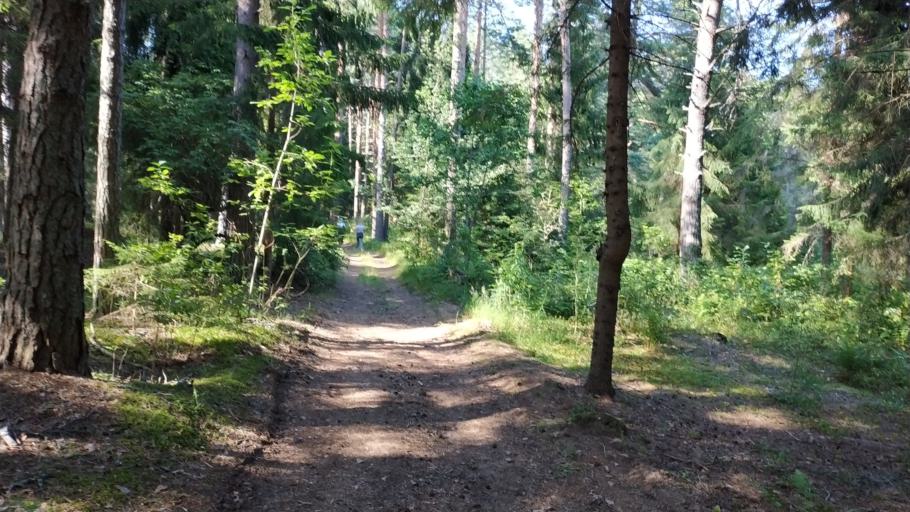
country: RU
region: Tverskaya
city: Ostashkov
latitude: 57.2469
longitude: 33.0495
